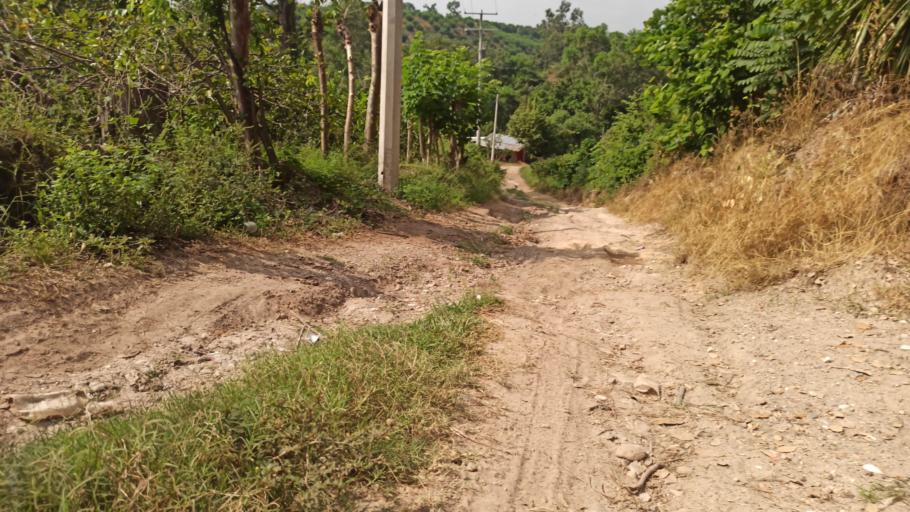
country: MX
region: Puebla
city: San Jose Acateno
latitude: 20.1592
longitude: -97.1815
